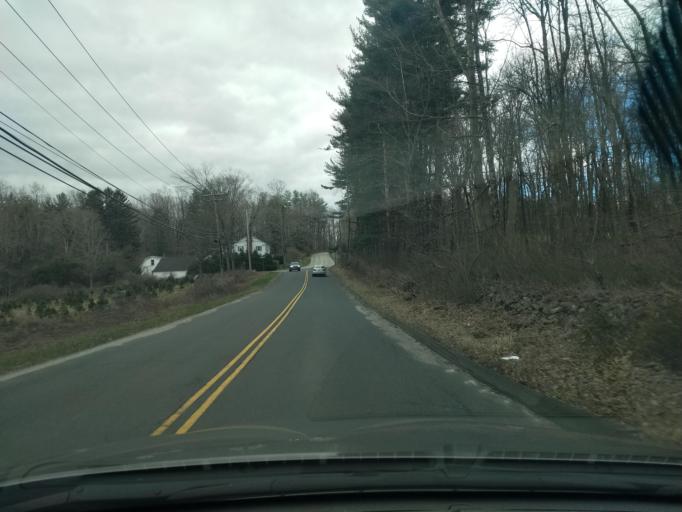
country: US
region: Connecticut
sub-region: Fairfield County
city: Newtown
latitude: 41.3691
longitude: -73.3331
